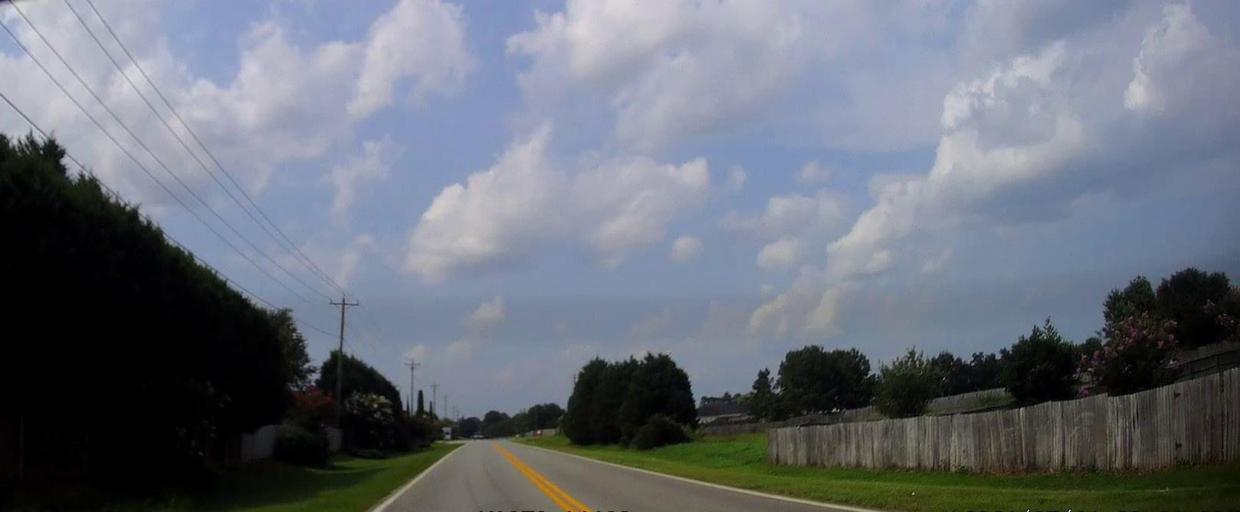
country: US
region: Georgia
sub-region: Houston County
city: Centerville
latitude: 32.5654
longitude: -83.6523
